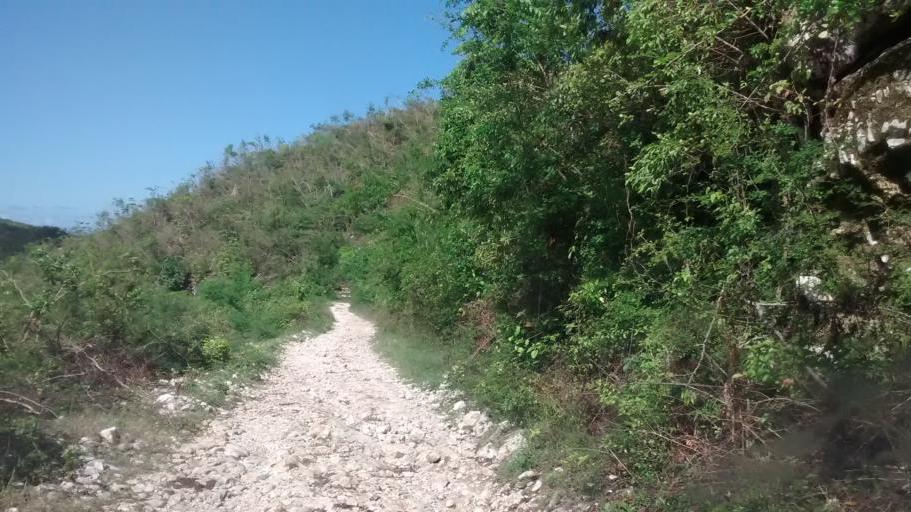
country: HT
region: Grandans
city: Corail
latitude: 18.5542
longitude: -73.9137
